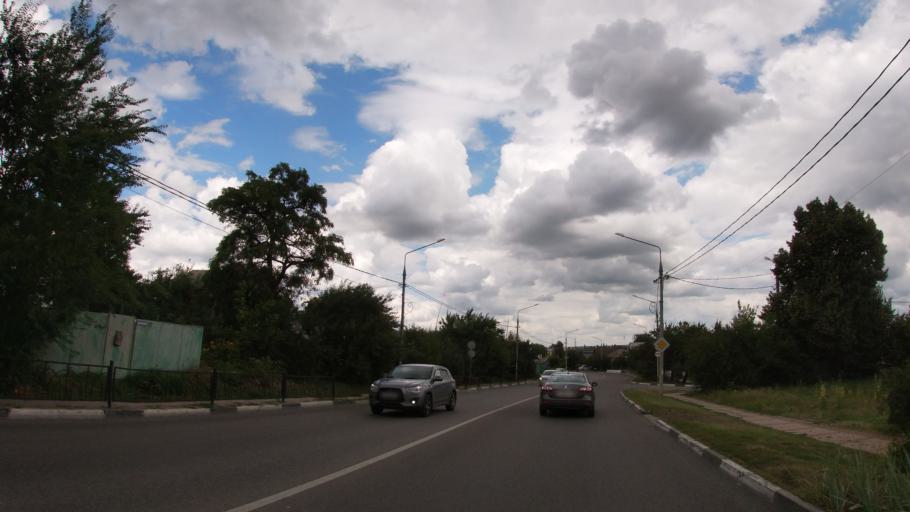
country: RU
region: Belgorod
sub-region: Belgorodskiy Rayon
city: Belgorod
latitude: 50.6063
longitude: 36.6118
